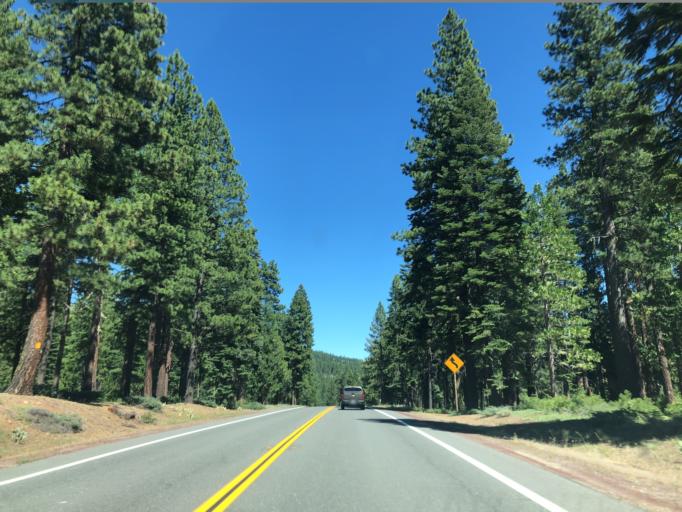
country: US
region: California
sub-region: Lassen County
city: Susanville
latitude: 40.4391
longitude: -120.8432
